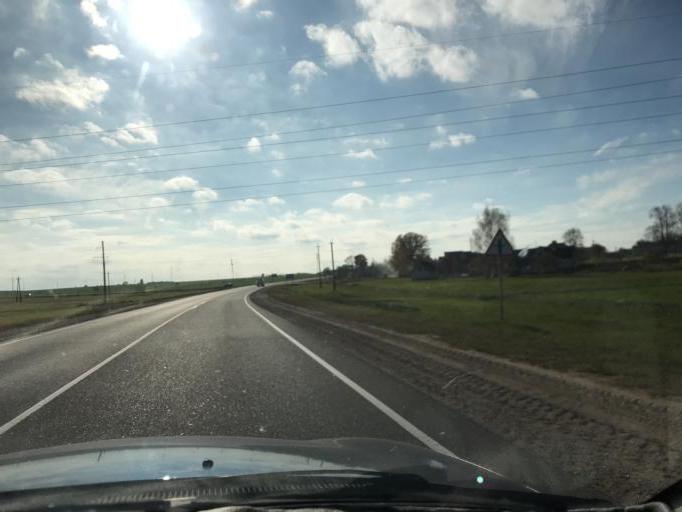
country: BY
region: Grodnenskaya
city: Voranava
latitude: 54.1482
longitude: 25.3267
